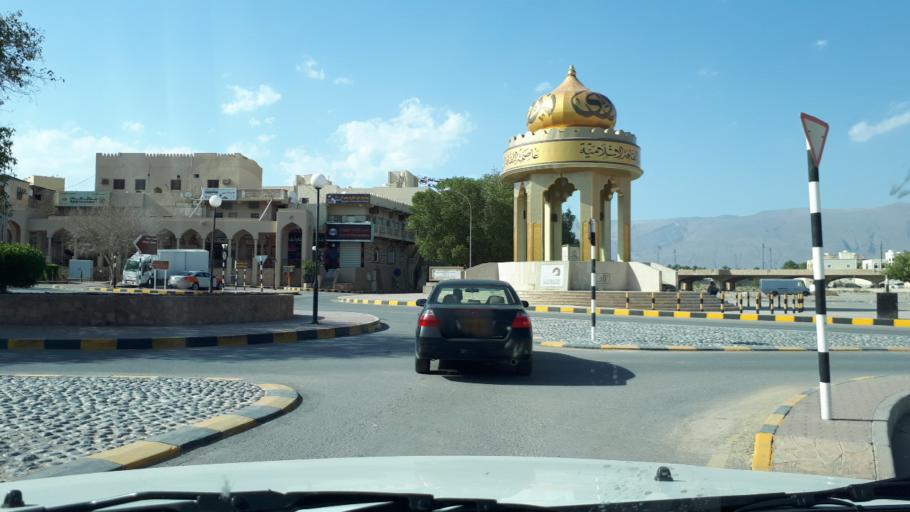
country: OM
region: Muhafazat ad Dakhiliyah
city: Nizwa
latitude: 22.9330
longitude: 57.5323
